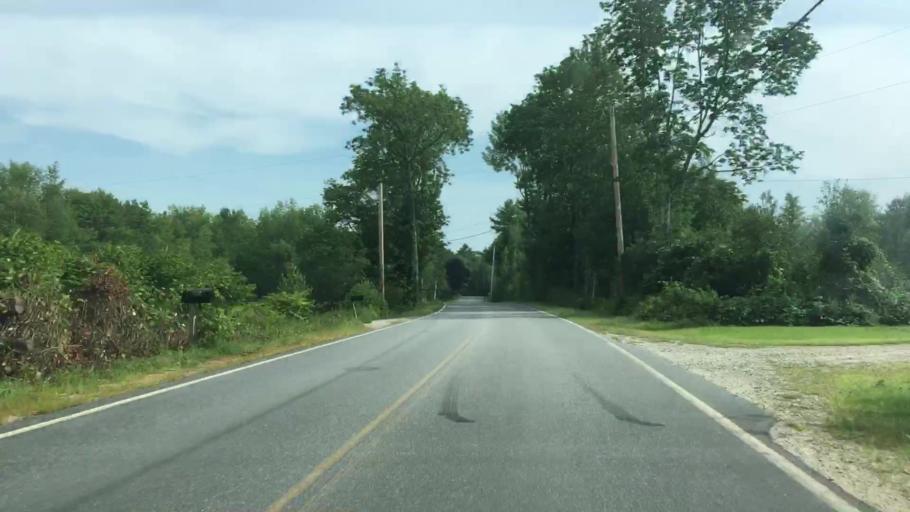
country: US
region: Maine
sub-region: Oxford County
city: Bethel
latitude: 44.2800
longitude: -70.7332
